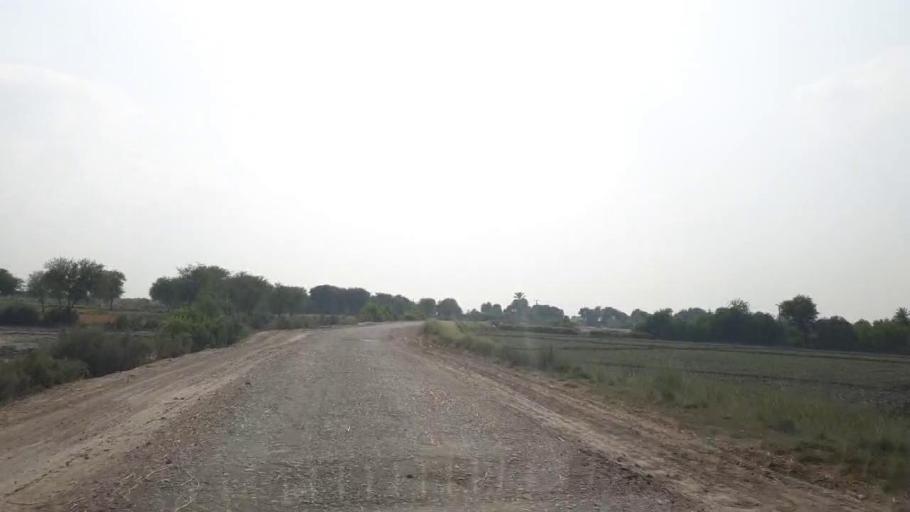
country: PK
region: Sindh
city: Rajo Khanani
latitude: 25.0280
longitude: 68.8042
